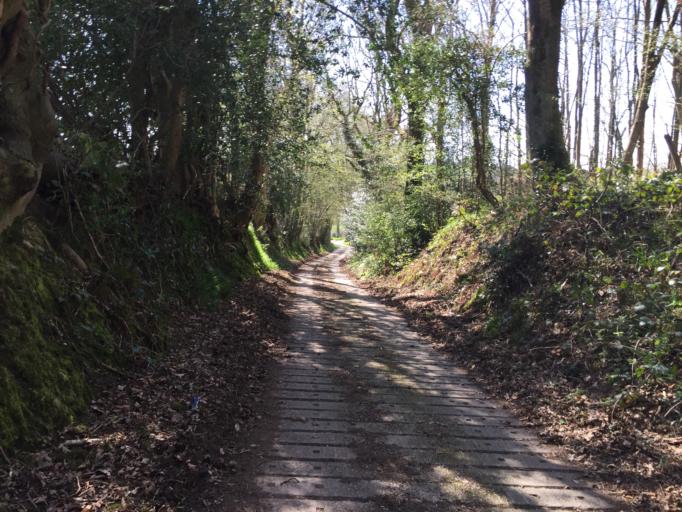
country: GB
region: England
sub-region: East Sussex
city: Wadhurst
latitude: 51.0259
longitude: 0.2908
